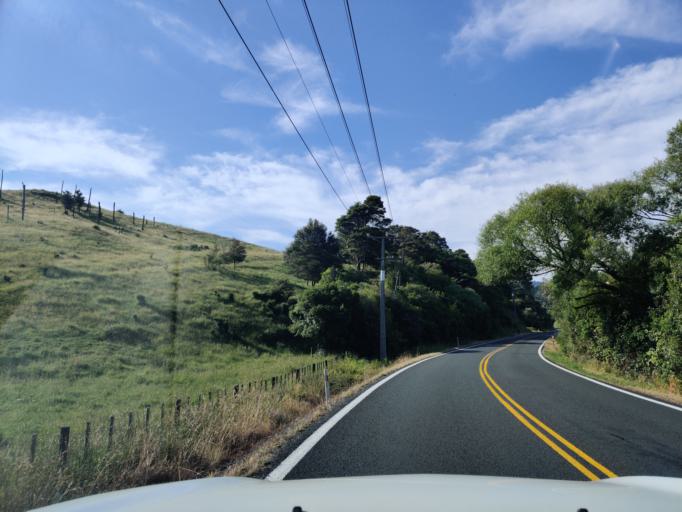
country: NZ
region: Waikato
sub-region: Waikato District
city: Ngaruawahia
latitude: -37.6579
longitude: 175.1422
